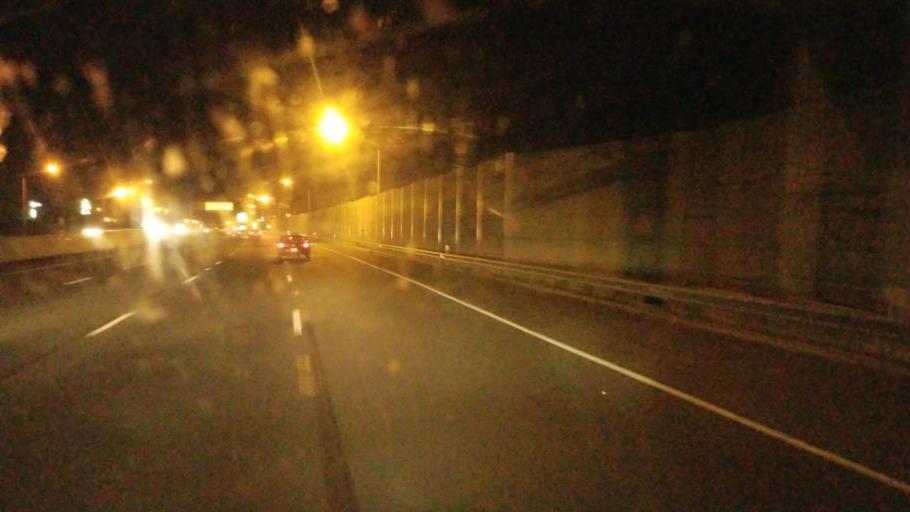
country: US
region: Indiana
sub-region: Allen County
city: Fort Wayne
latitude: 41.1727
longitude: -85.1031
